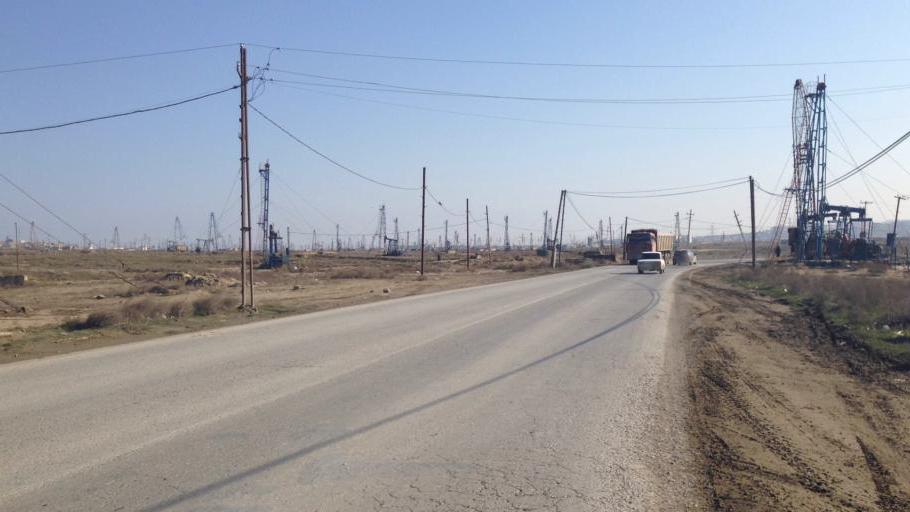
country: AZ
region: Baki
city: Balakhani
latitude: 40.4566
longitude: 49.8929
